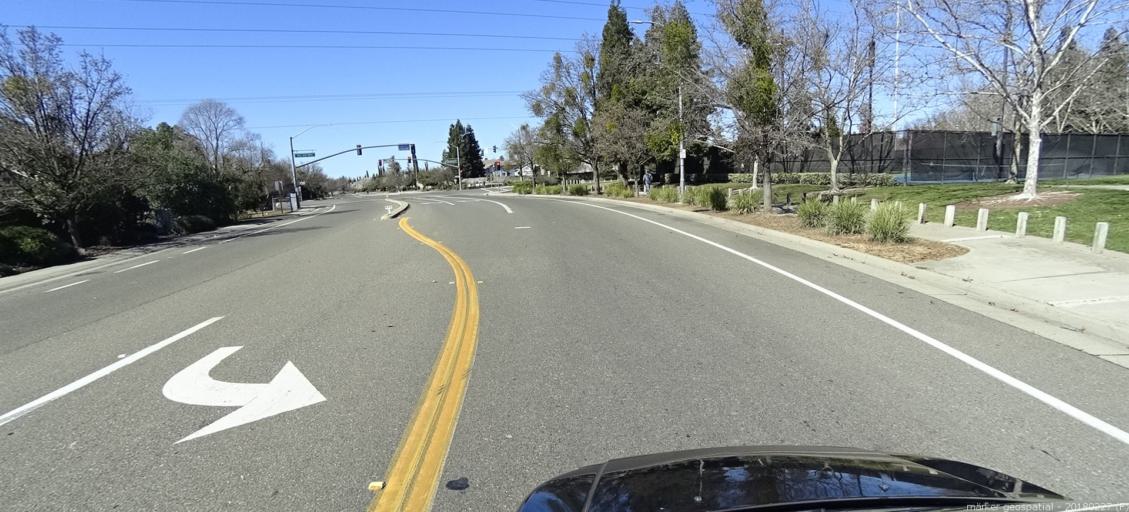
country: US
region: California
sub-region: Sacramento County
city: Antelope
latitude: 38.7181
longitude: -121.3454
